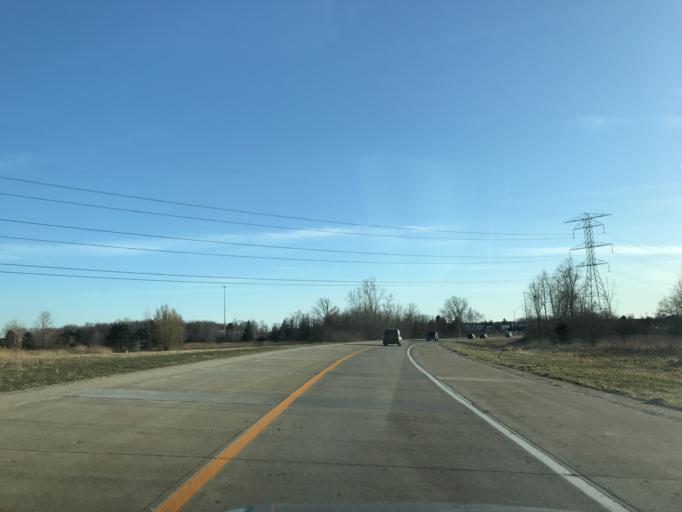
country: US
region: Michigan
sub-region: Oakland County
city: Novi
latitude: 42.4881
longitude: -83.4496
